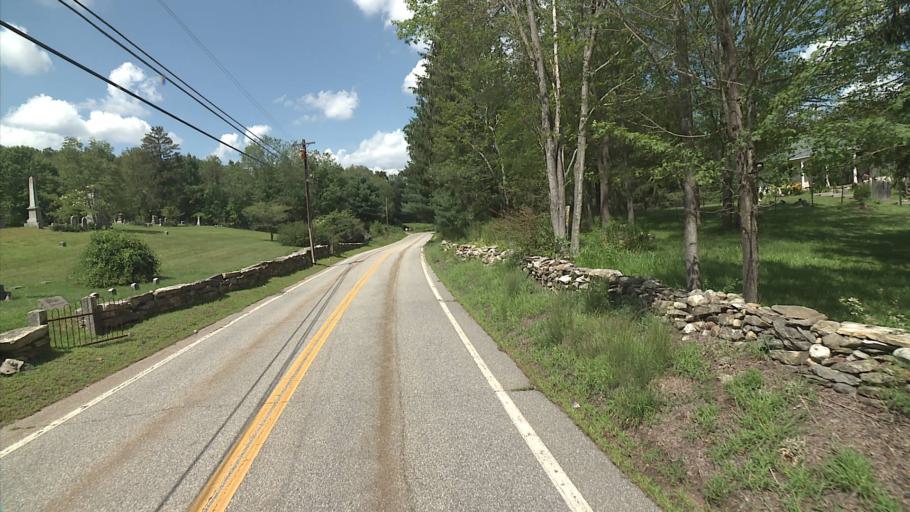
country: US
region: Connecticut
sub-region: Tolland County
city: Storrs
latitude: 41.8184
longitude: -72.1722
